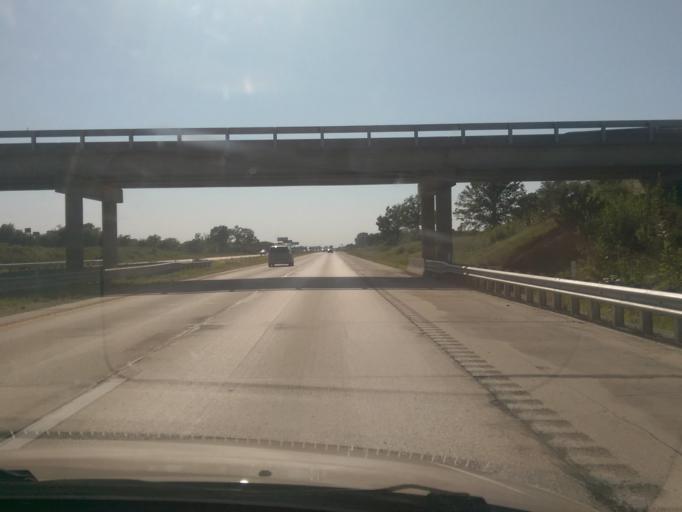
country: US
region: Missouri
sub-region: Saline County
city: Sweet Springs
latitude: 38.9736
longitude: -93.3311
